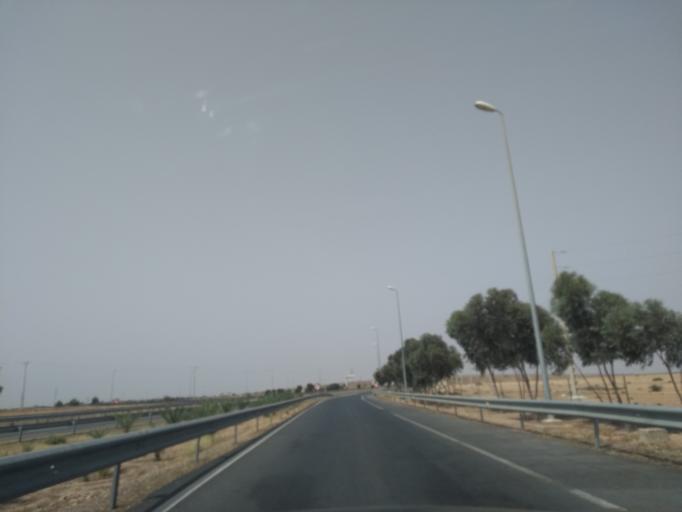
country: MA
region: Marrakech-Tensift-Al Haouz
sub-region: Marrakech
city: Marrakesh
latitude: 31.7189
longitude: -8.2360
